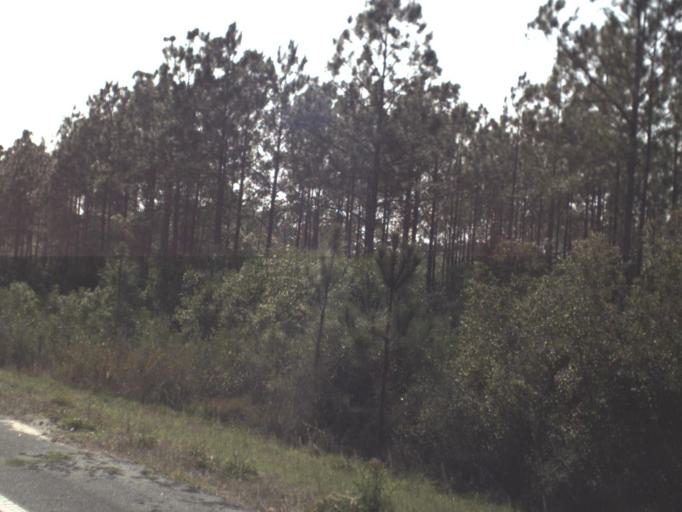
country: US
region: Florida
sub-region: Franklin County
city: Carrabelle
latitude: 29.9246
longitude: -84.5199
